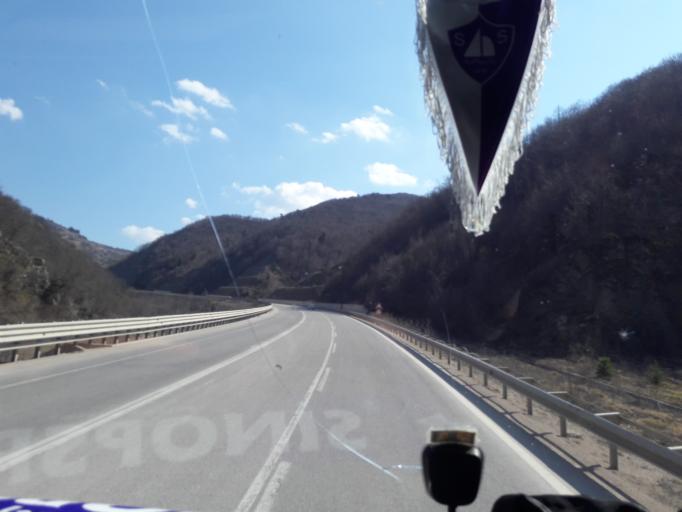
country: TR
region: Sinop
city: Erfelek
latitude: 41.6822
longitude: 34.9085
